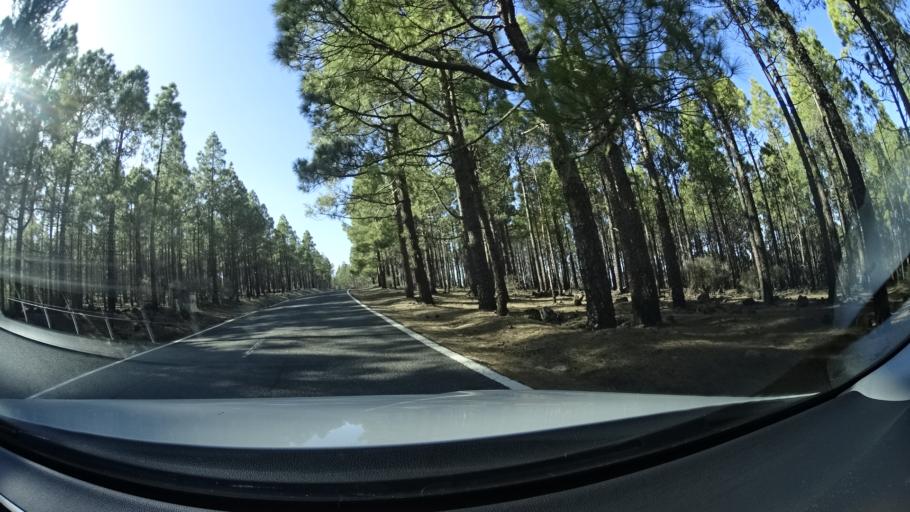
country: ES
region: Canary Islands
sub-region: Provincia de Las Palmas
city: San Bartolome
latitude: 27.9638
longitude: -15.5518
